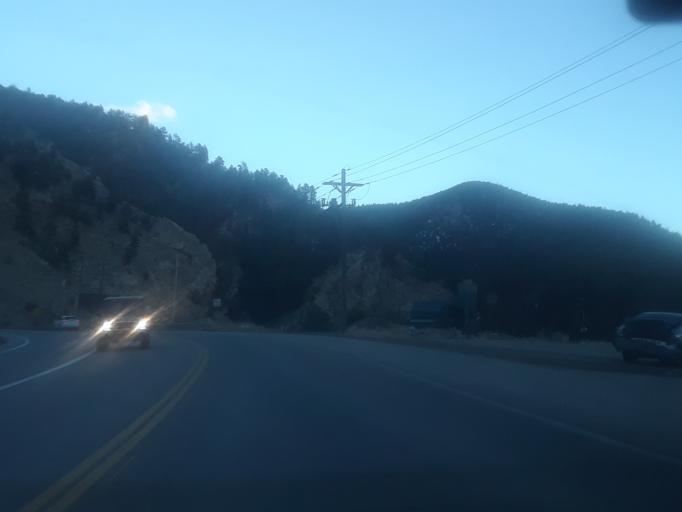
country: US
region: Colorado
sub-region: Clear Creek County
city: Idaho Springs
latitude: 39.7425
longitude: -105.4311
